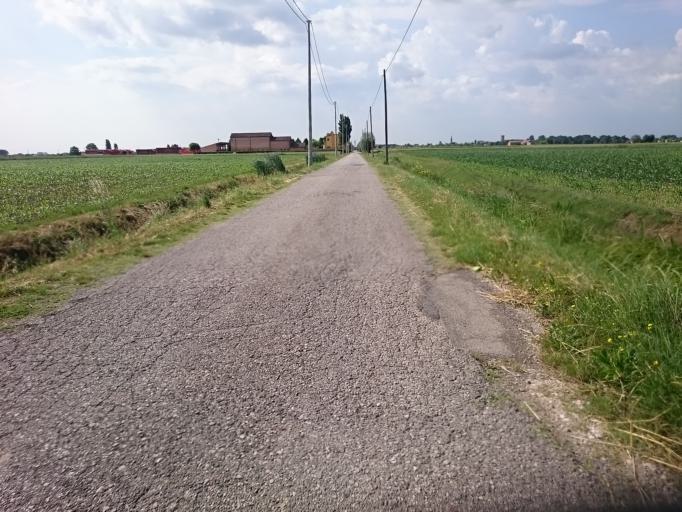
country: IT
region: Veneto
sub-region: Provincia di Padova
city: Montagnana
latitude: 45.2146
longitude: 11.4781
